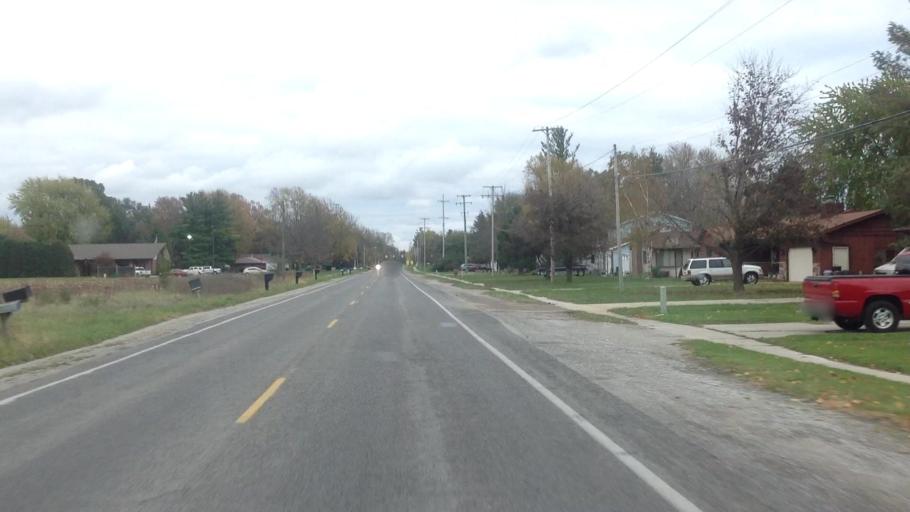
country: US
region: Michigan
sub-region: Saginaw County
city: Bridgeport
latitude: 43.3743
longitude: -83.9089
